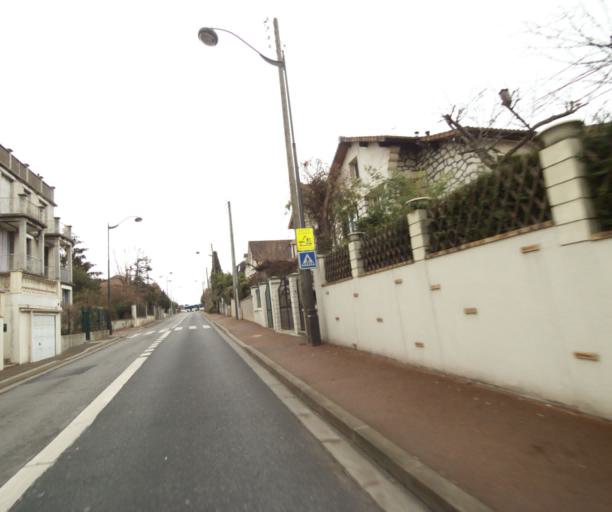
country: FR
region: Ile-de-France
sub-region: Departement des Hauts-de-Seine
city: Rueil-Malmaison
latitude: 48.8687
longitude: 2.1743
